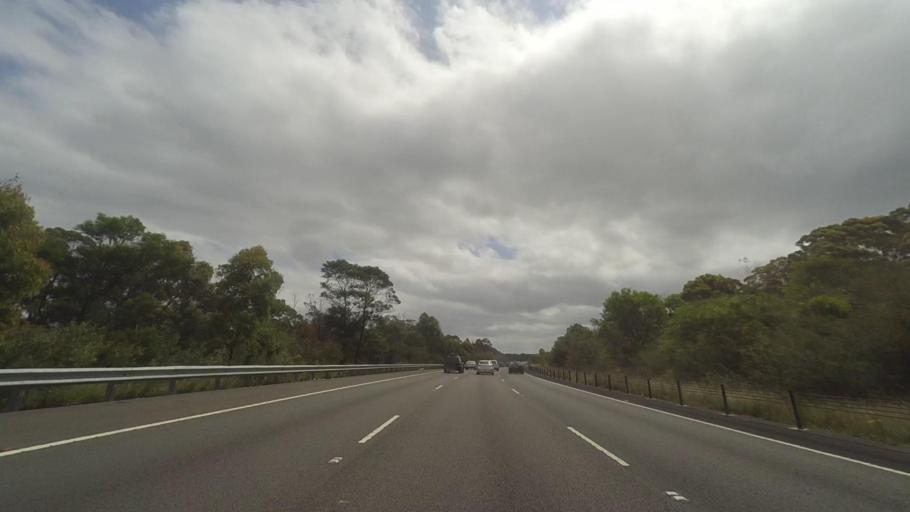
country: AU
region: New South Wales
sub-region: Gosford Shire
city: Point Clare
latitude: -33.4511
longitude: 151.2155
